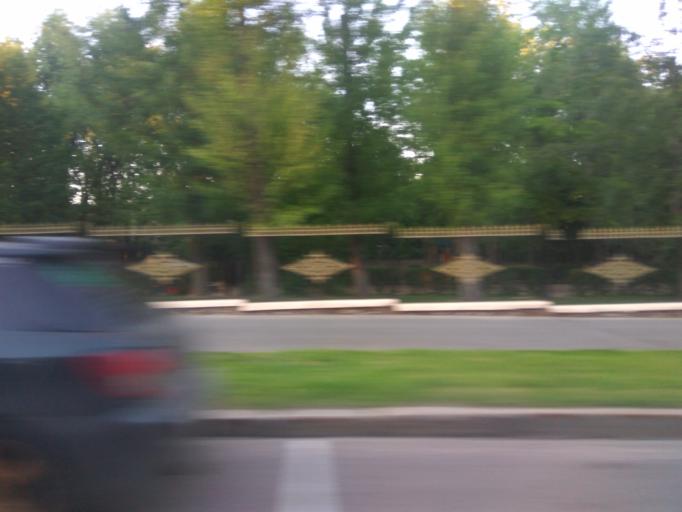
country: RU
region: Moscow
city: Vorob'yovo
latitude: 55.7129
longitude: 37.5260
